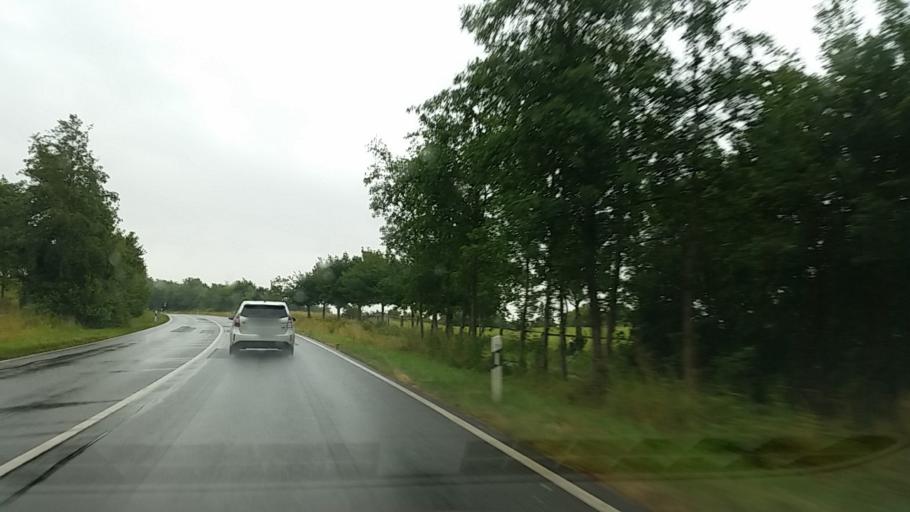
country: DE
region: Mecklenburg-Vorpommern
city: Kropelin
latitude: 54.0749
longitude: 11.8040
